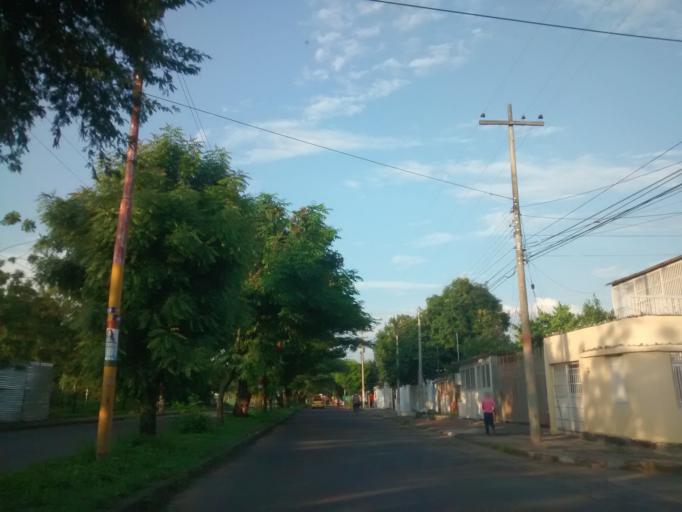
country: CO
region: Cundinamarca
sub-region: Girardot
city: Girardot City
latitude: 4.3086
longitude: -74.7943
